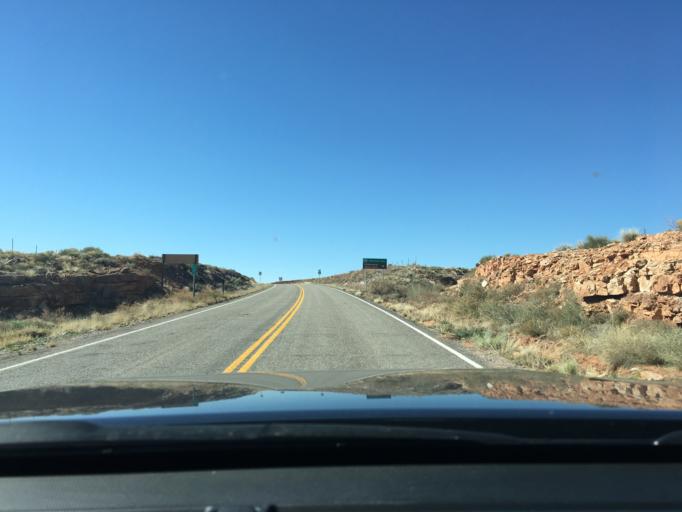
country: US
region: Utah
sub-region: San Juan County
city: Blanding
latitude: 37.1978
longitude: -109.8646
